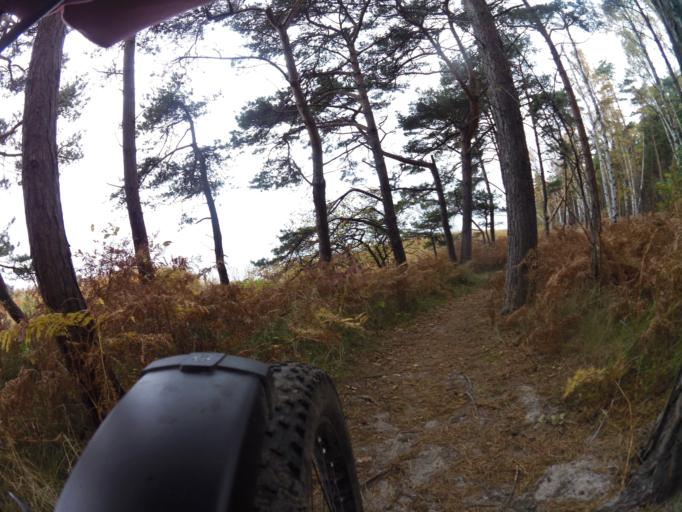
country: PL
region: Pomeranian Voivodeship
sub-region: Powiat pucki
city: Jastarnia
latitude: 54.6878
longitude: 18.7016
